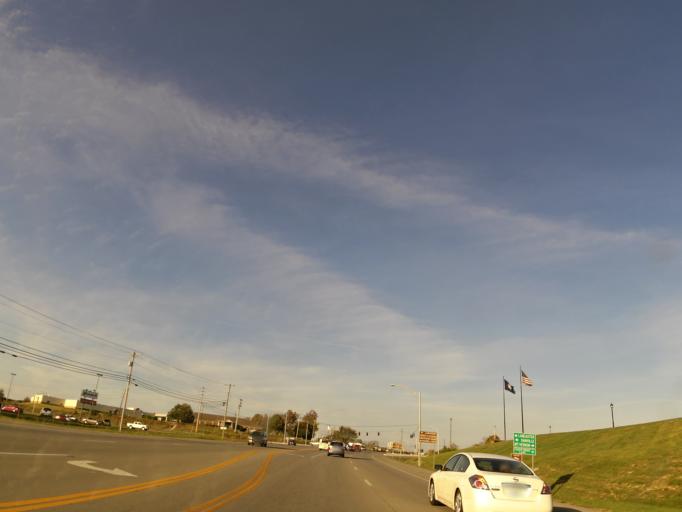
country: US
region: Kentucky
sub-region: Lincoln County
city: Stanford
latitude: 37.5392
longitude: -84.6529
